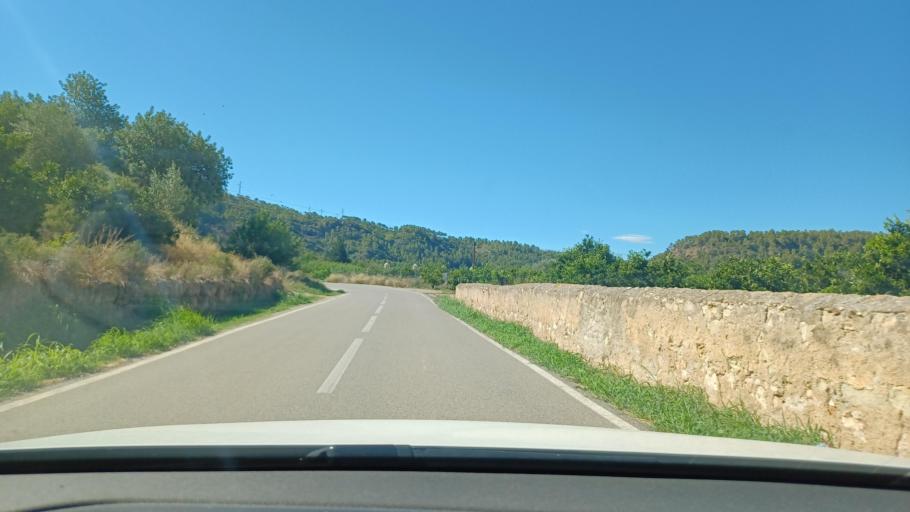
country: ES
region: Catalonia
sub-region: Provincia de Tarragona
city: Benifallet
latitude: 40.9679
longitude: 0.5143
